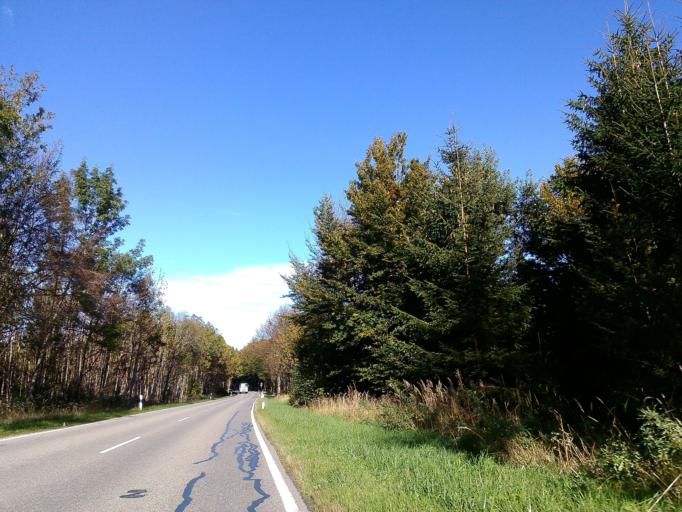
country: DE
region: Bavaria
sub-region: Upper Bavaria
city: Starnberg
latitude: 48.0276
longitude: 11.3043
